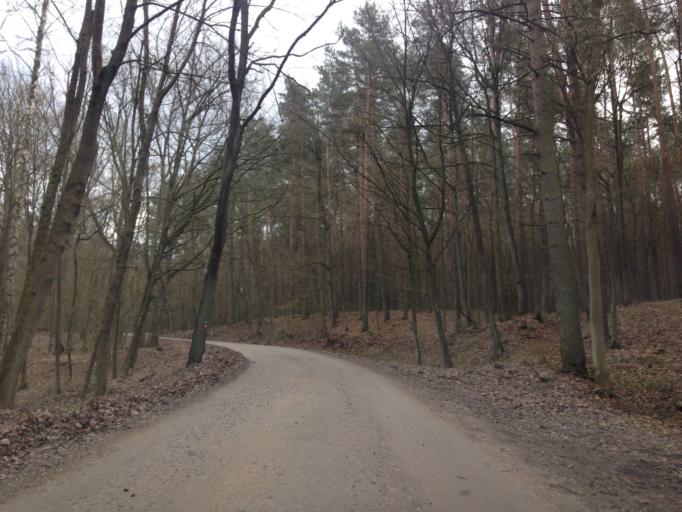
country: PL
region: Kujawsko-Pomorskie
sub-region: Powiat brodnicki
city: Gorzno
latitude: 53.2196
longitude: 19.6730
